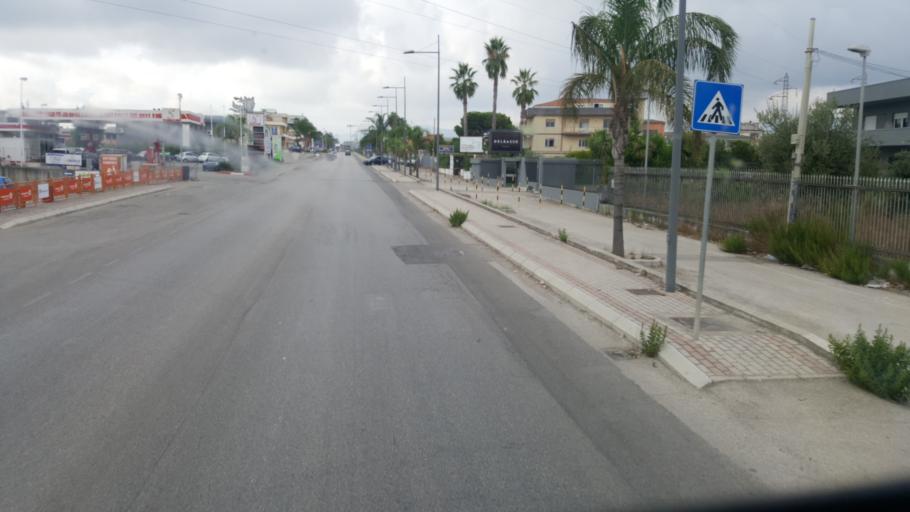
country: IT
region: Campania
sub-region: Provincia di Salerno
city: Battipaglia
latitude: 40.5968
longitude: 14.9888
